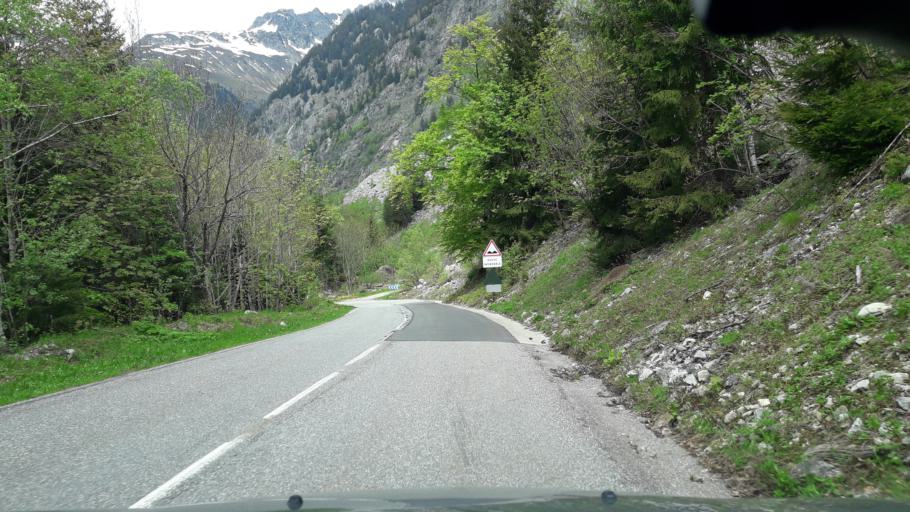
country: FR
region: Rhone-Alpes
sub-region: Departement de l'Isere
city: Huez
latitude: 45.2039
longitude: 6.0743
